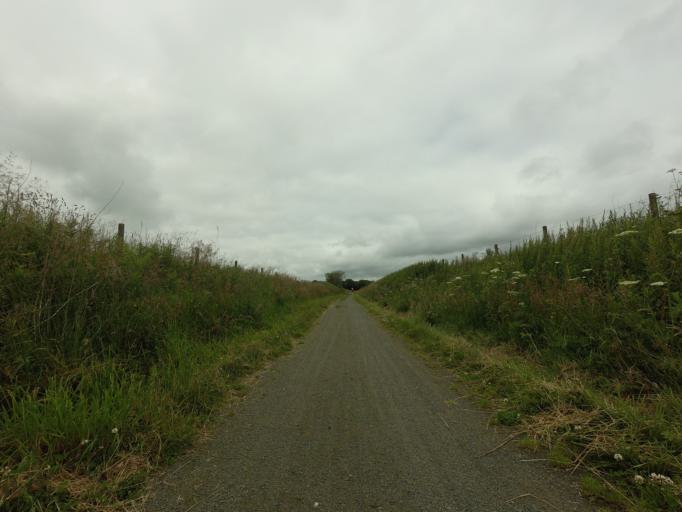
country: GB
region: Scotland
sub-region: Aberdeenshire
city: Ellon
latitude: 57.4847
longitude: -2.1351
